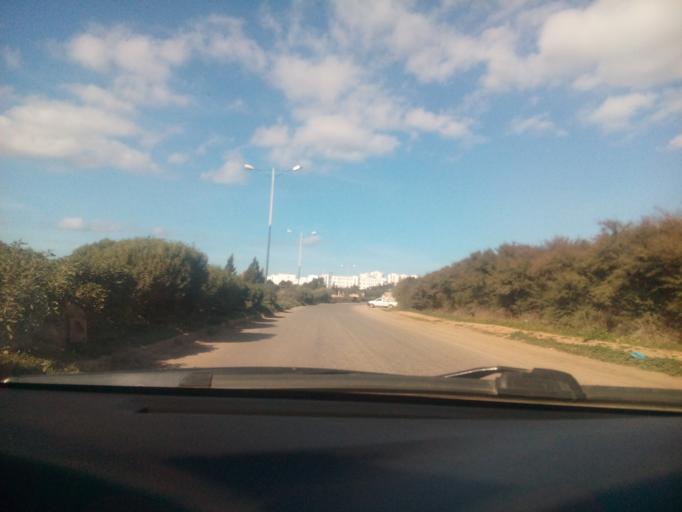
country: DZ
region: Oran
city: Bir el Djir
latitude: 35.6879
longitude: -0.5746
